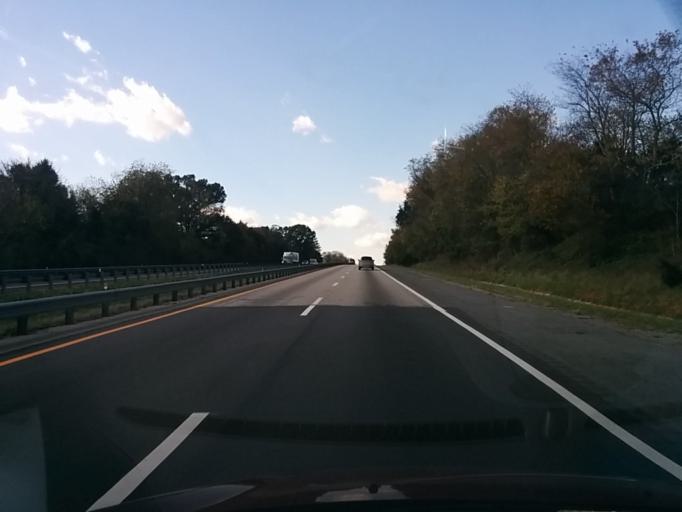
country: US
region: Virginia
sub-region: Botetourt County
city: Buchanan
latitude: 37.5226
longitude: -79.7124
